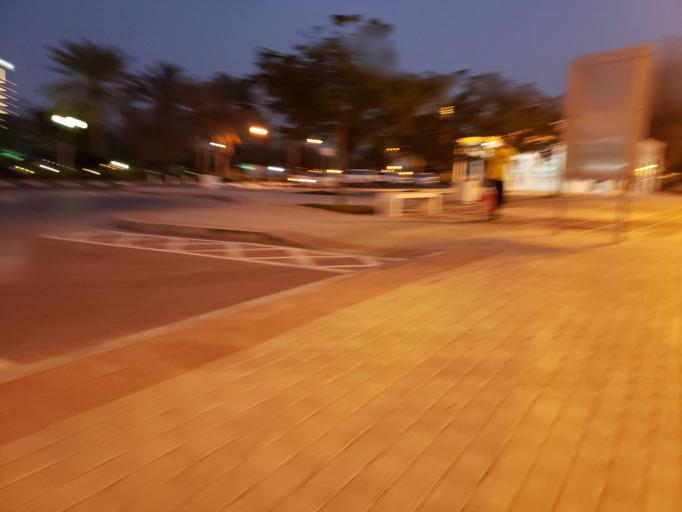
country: AE
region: Ash Shariqah
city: Sharjah
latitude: 25.3243
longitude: 55.3515
